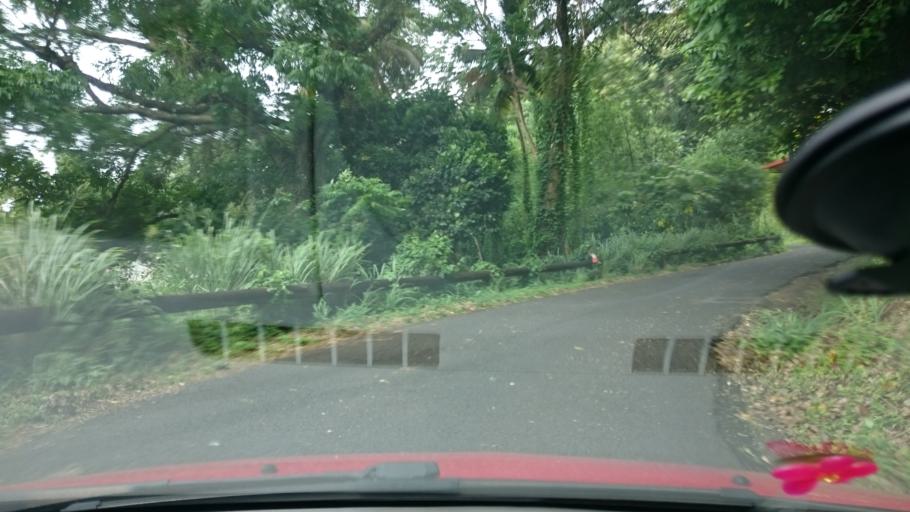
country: MQ
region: Martinique
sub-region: Martinique
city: Riviere-Pilote
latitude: 14.4982
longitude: -60.9206
